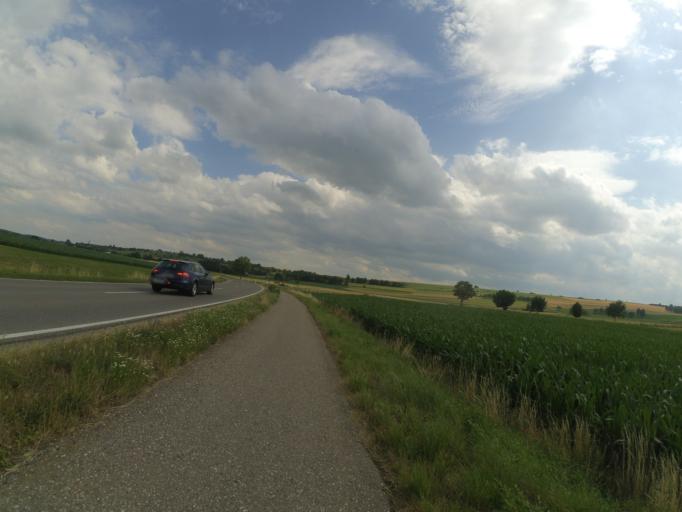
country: DE
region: Baden-Wuerttemberg
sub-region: Tuebingen Region
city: Griesingen
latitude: 48.2764
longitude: 9.7626
